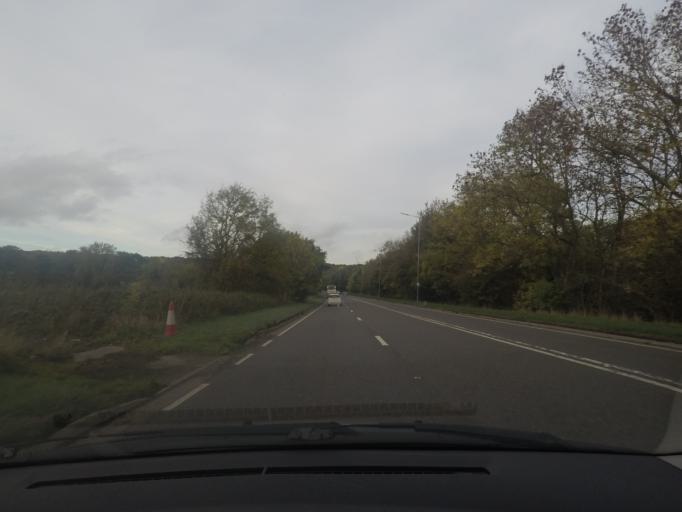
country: GB
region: England
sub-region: Sheffield
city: Chapletown
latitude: 53.4793
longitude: -1.4969
